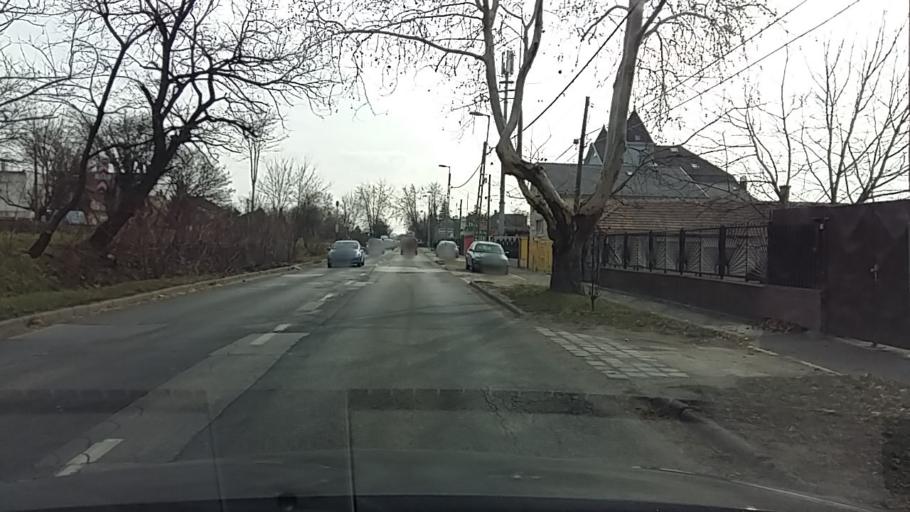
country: HU
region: Budapest
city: Budapest XVIII. keruelet
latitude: 47.4100
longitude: 19.1780
